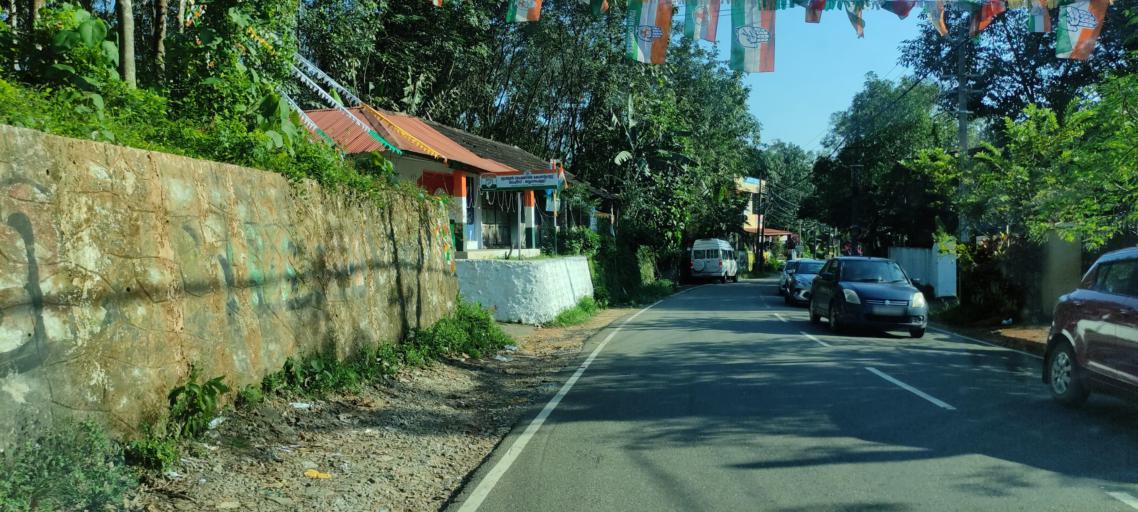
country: IN
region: Kerala
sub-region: Pattanamtitta
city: Adur
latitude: 9.1743
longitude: 76.7415
